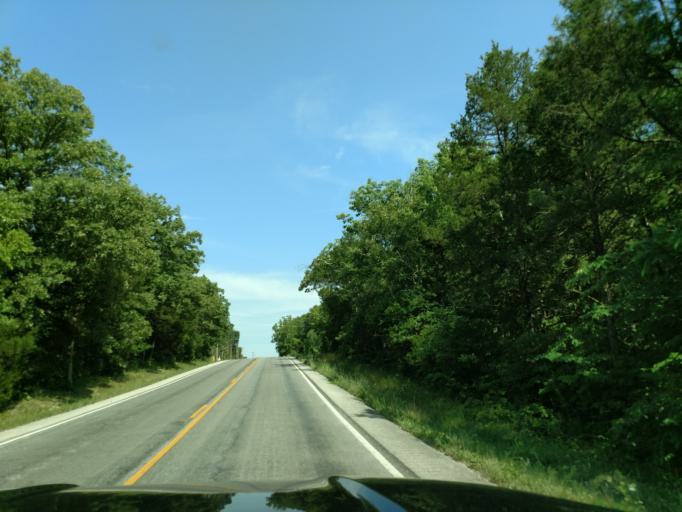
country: US
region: Missouri
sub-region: Barry County
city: Shell Knob
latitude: 36.6141
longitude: -93.5969
